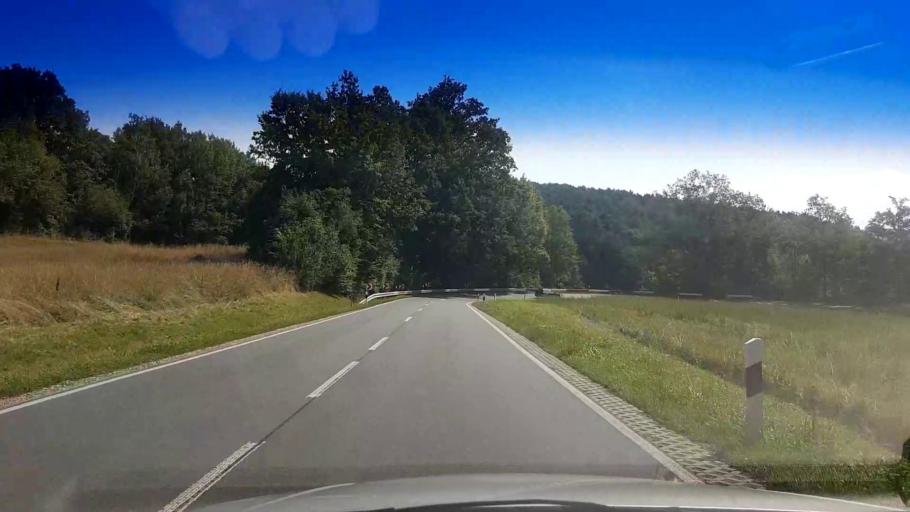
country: DE
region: Bavaria
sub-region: Upper Franconia
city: Eckersdorf
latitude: 49.9365
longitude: 11.5213
